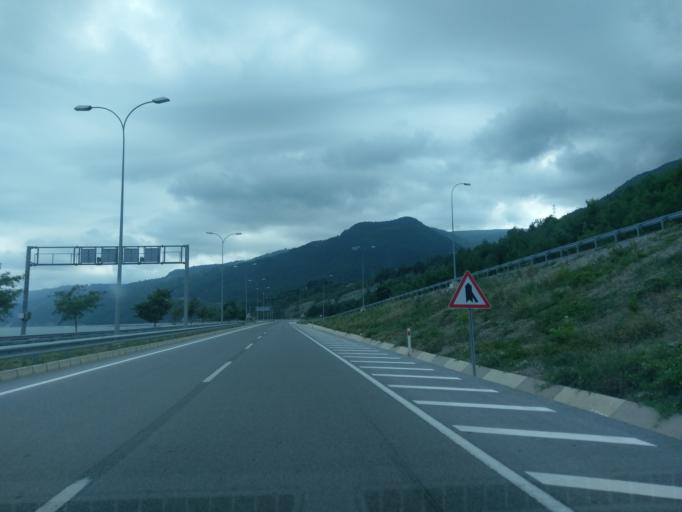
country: TR
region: Sinop
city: Dikmen
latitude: 41.7265
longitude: 35.2643
